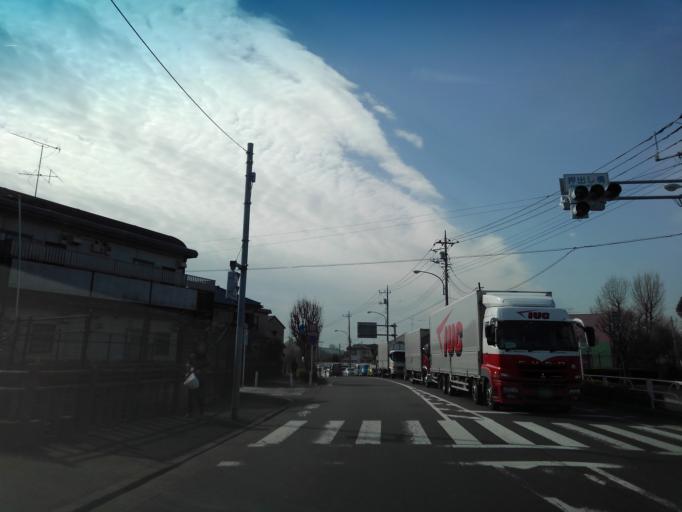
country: JP
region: Tokyo
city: Tanashicho
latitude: 35.7625
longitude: 139.5093
